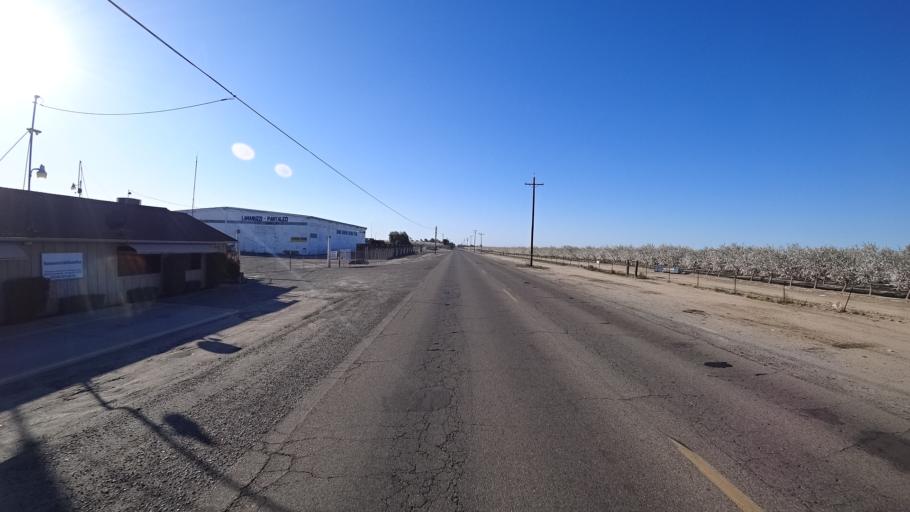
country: US
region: California
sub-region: Fresno County
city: Biola
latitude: 36.7883
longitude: -119.9163
